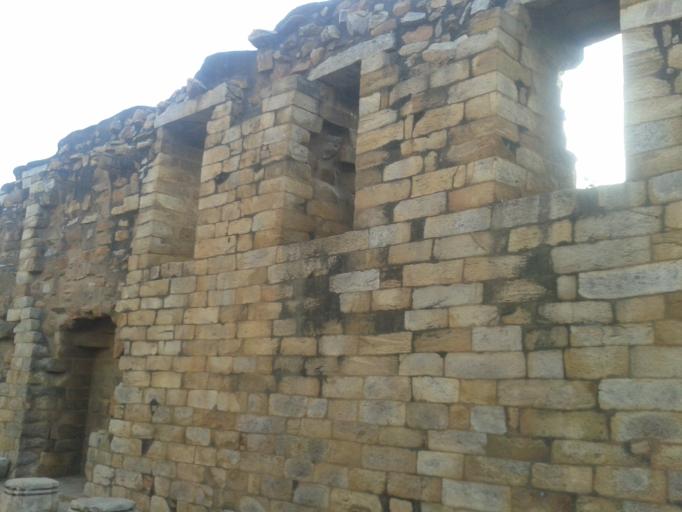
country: IN
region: NCT
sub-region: New Delhi
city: New Delhi
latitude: 28.5251
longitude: 77.1848
